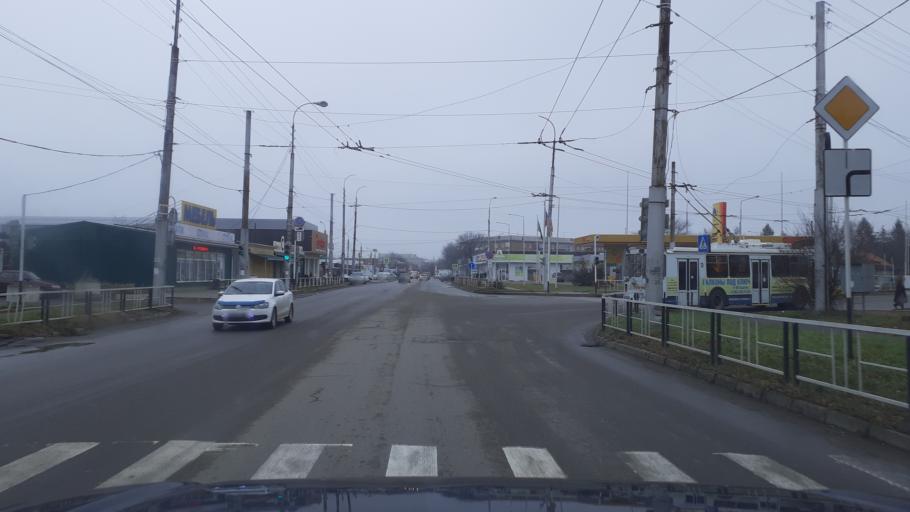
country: RU
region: Adygeya
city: Maykop
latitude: 44.6246
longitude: 40.0714
